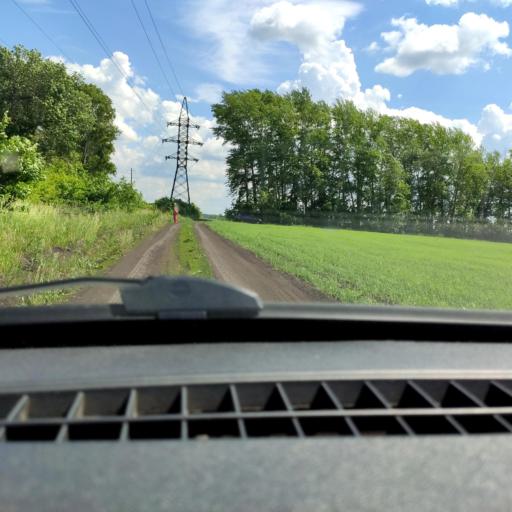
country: RU
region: Bashkortostan
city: Kabakovo
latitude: 54.5186
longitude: 56.0812
